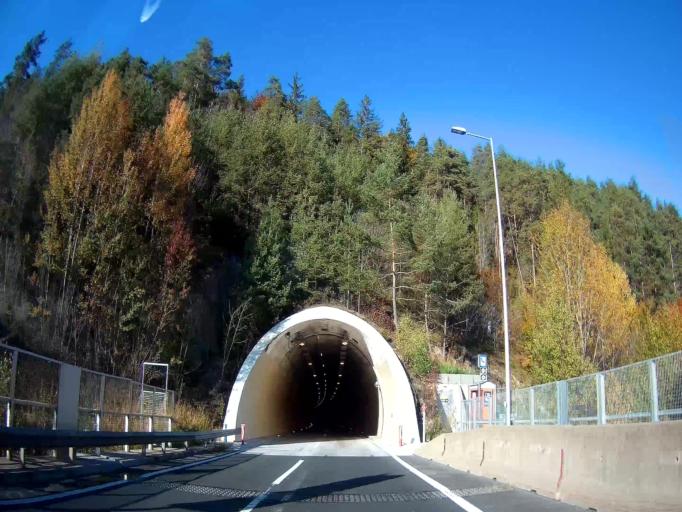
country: AT
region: Carinthia
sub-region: Politischer Bezirk Wolfsberg
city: Sankt Andrae
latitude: 46.7260
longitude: 14.8001
